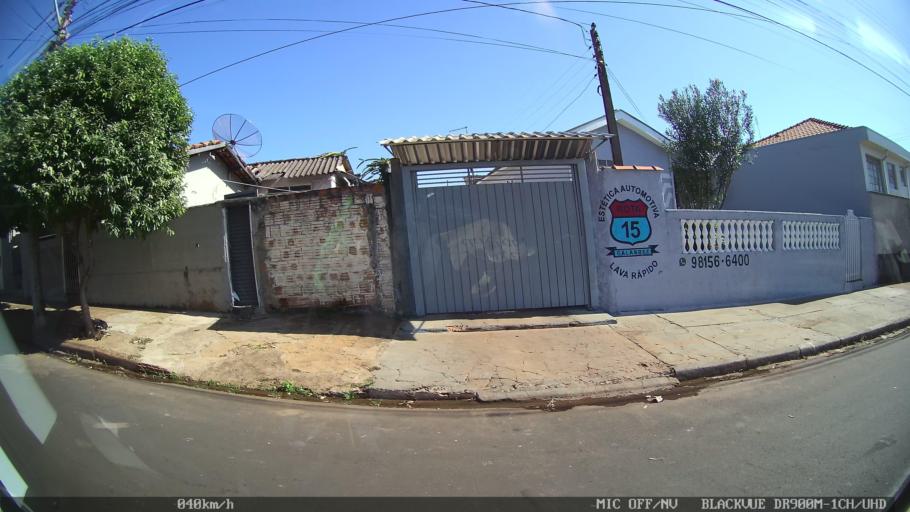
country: BR
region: Sao Paulo
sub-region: Batatais
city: Batatais
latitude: -20.8948
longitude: -47.5818
